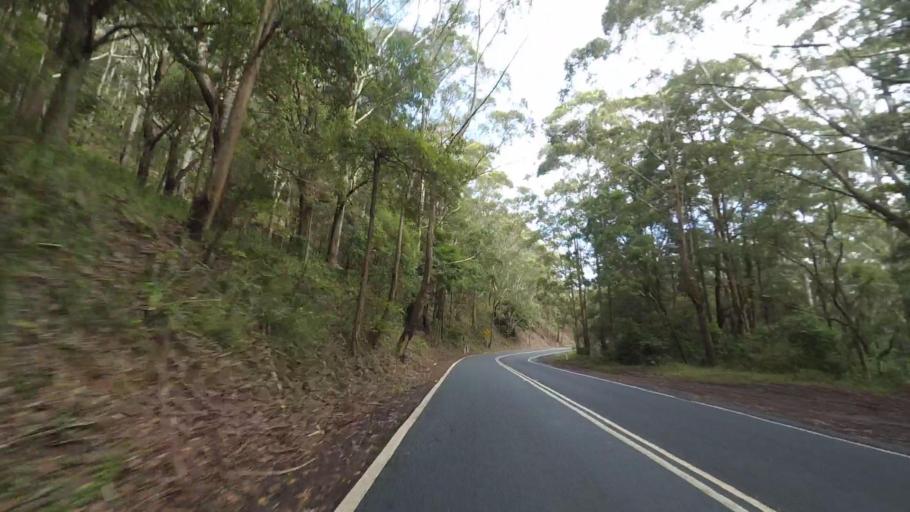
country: AU
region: New South Wales
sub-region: Wollongong
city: Helensburgh
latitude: -34.2065
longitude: 151.0114
